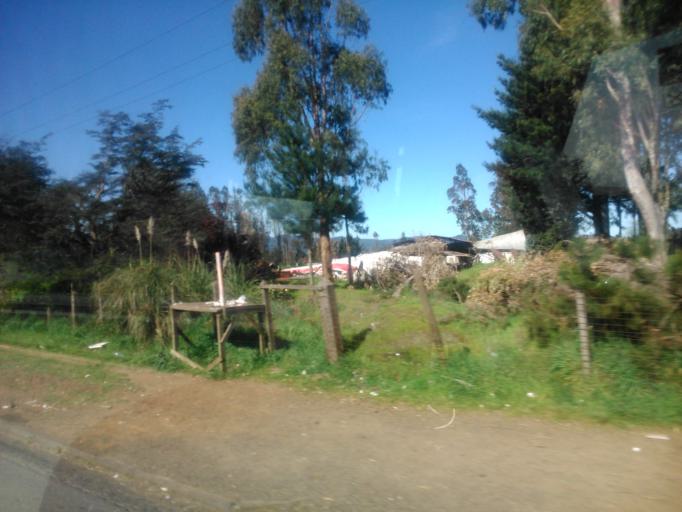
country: CL
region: Araucania
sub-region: Provincia de Cautin
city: Temuco
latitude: -38.7990
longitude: -72.6229
